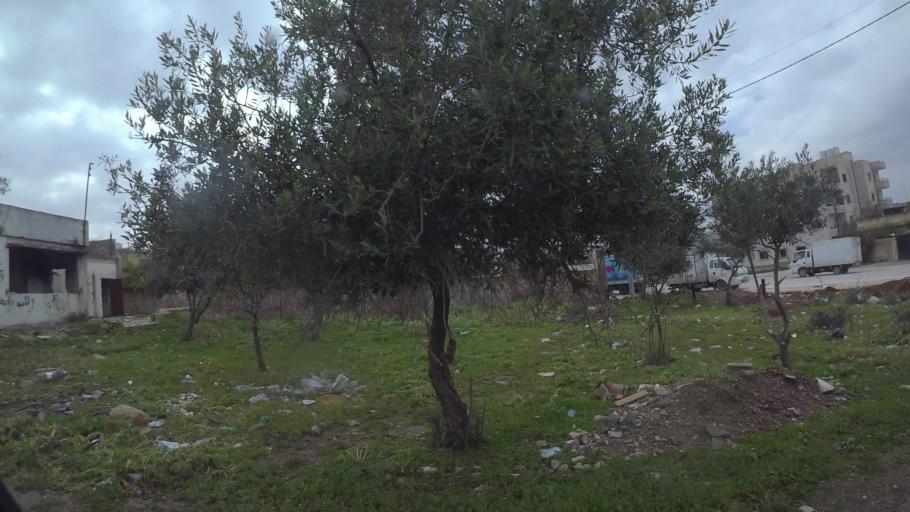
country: JO
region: Amman
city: Al Jubayhah
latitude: 32.0535
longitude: 35.8419
